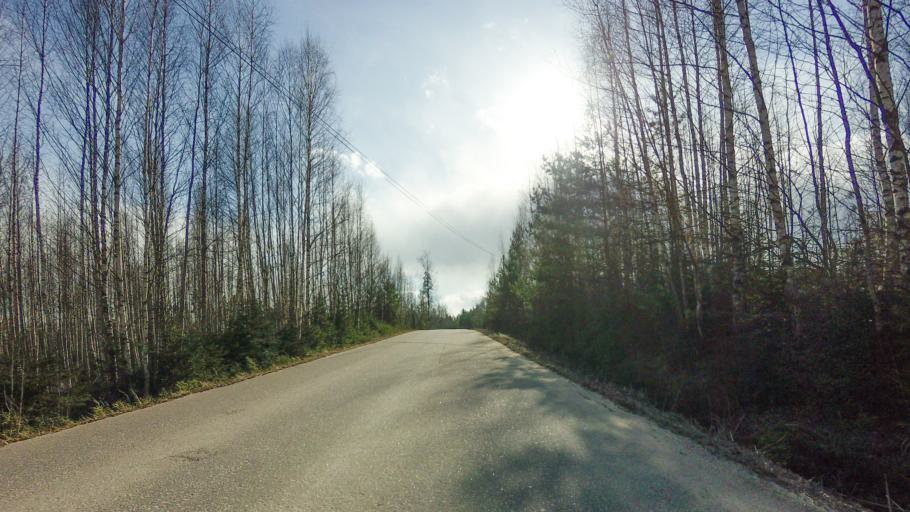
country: FI
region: Varsinais-Suomi
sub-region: Salo
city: Suomusjaervi
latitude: 60.3017
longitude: 23.6447
